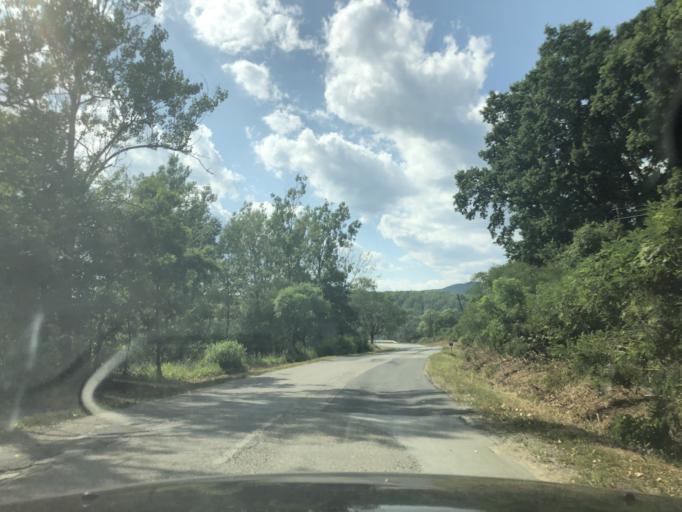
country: HU
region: Borsod-Abauj-Zemplen
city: Szendro
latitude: 48.4553
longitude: 20.7741
